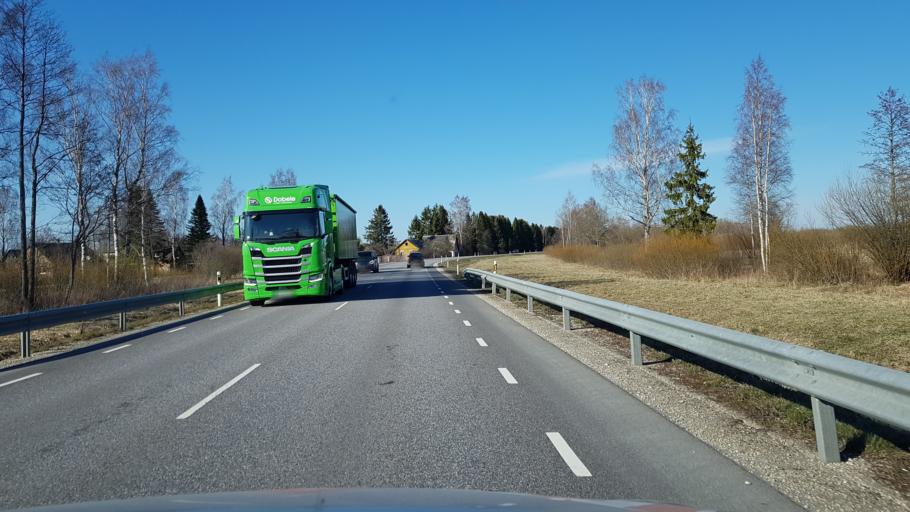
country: EE
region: Jogevamaa
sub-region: Mustvee linn
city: Mustvee
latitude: 58.9128
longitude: 27.0033
